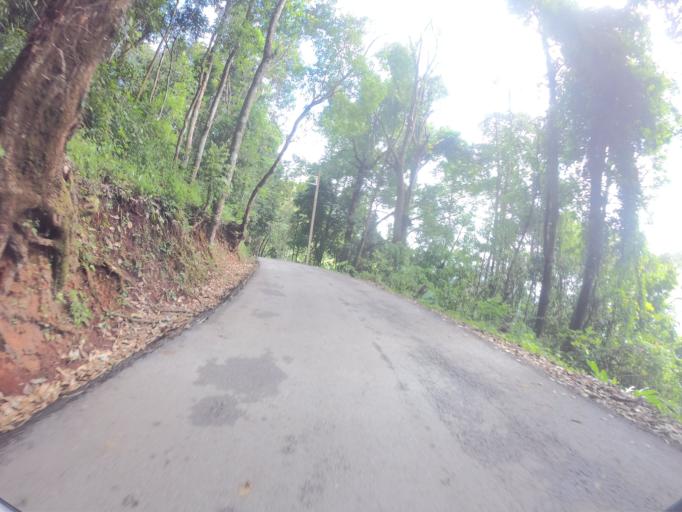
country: TH
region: Chiang Mai
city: Chiang Mai
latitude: 18.8137
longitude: 98.8829
